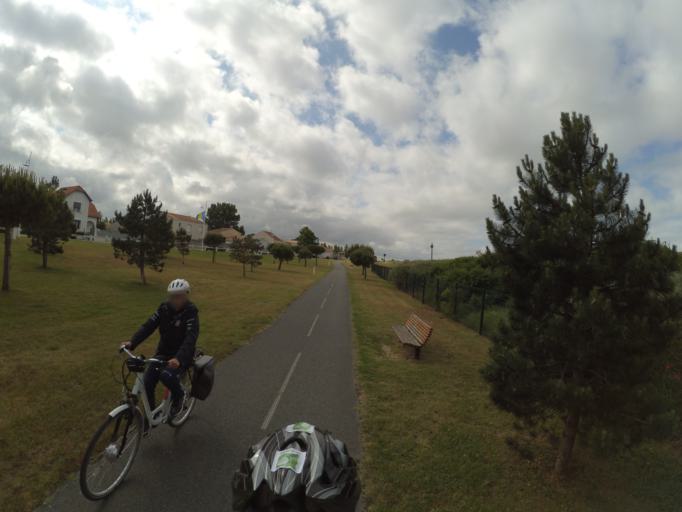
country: FR
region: Poitou-Charentes
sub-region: Departement de la Charente-Maritime
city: Angoulins
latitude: 46.0941
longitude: -1.1000
